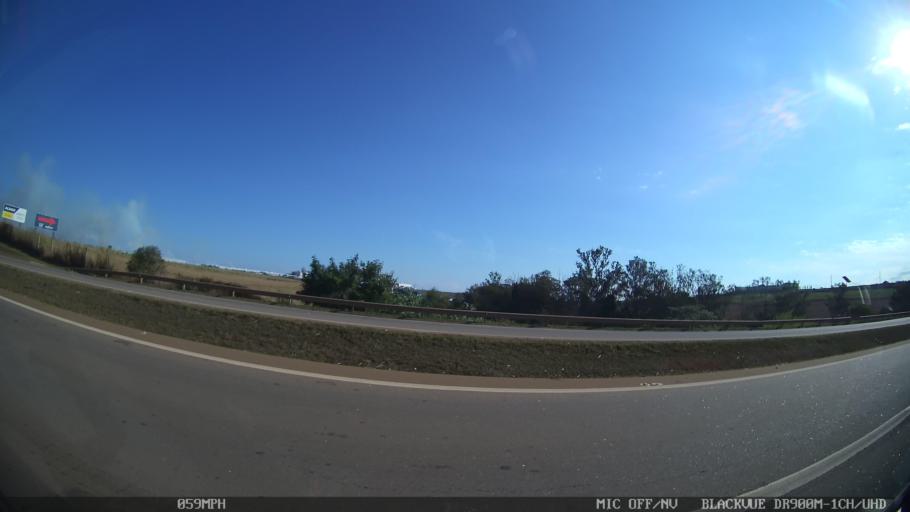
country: BR
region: Sao Paulo
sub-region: Piracicaba
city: Piracicaba
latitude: -22.6770
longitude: -47.5976
